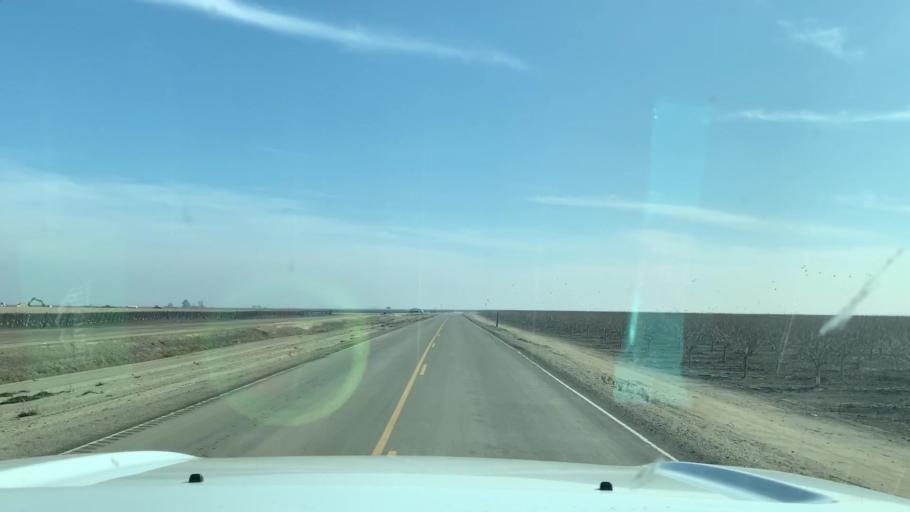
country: US
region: California
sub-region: Kern County
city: Buttonwillow
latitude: 35.4546
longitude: -119.5699
